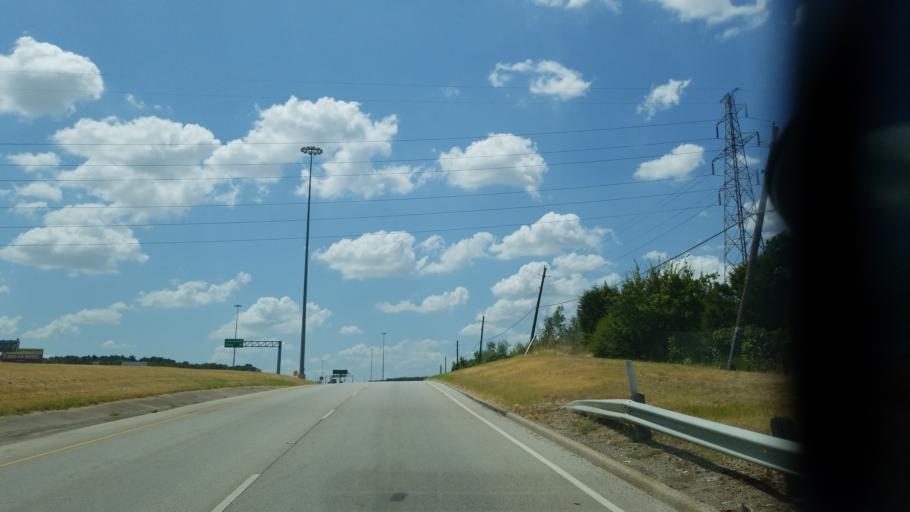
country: US
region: Texas
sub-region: Dallas County
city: Cockrell Hill
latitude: 32.7428
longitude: -96.9197
